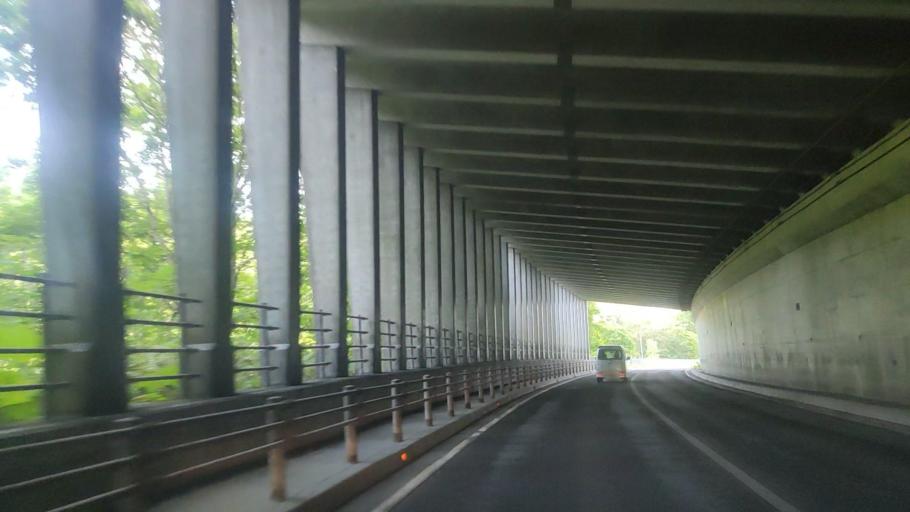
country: JP
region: Hokkaido
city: Iwamizawa
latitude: 43.0146
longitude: 142.0028
